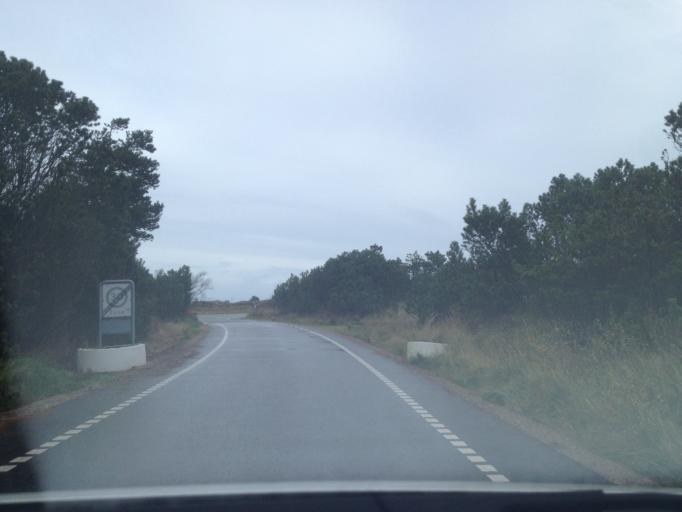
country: DE
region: Schleswig-Holstein
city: List
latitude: 55.1582
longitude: 8.5189
